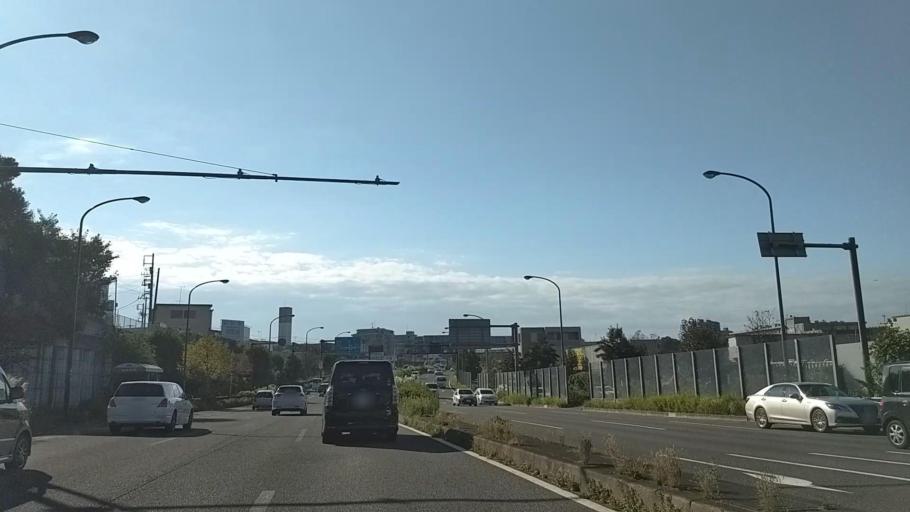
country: JP
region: Kanagawa
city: Yokohama
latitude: 35.4570
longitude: 139.5632
